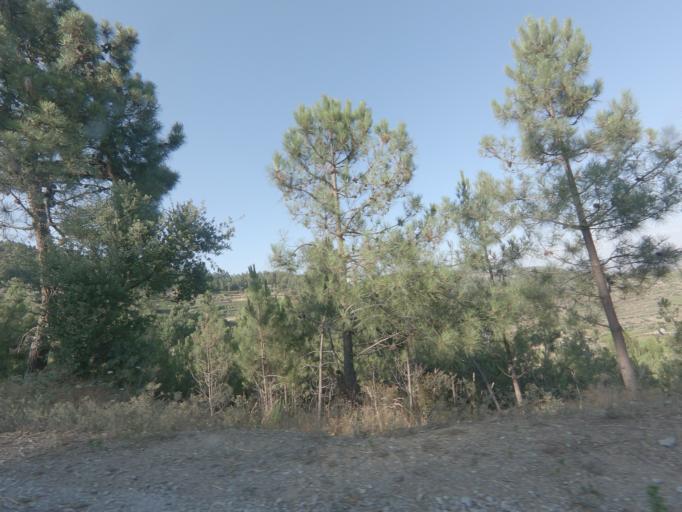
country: PT
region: Vila Real
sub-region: Sabrosa
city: Vilela
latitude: 41.1858
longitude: -7.6076
